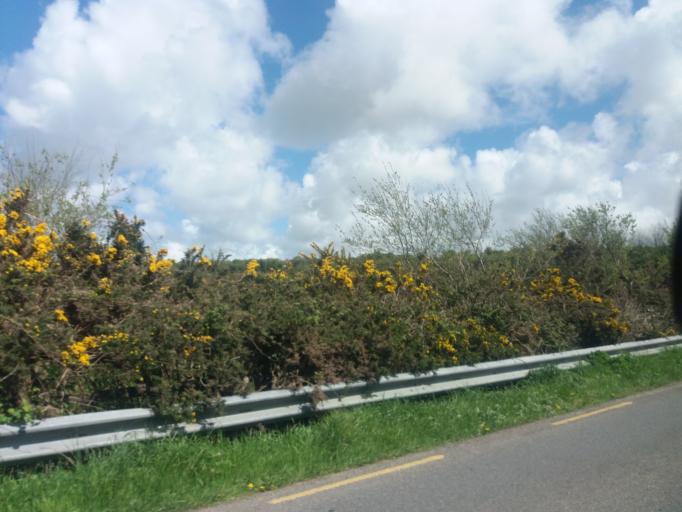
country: IE
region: Leinster
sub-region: Loch Garman
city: New Ross
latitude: 52.2675
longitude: -6.7745
